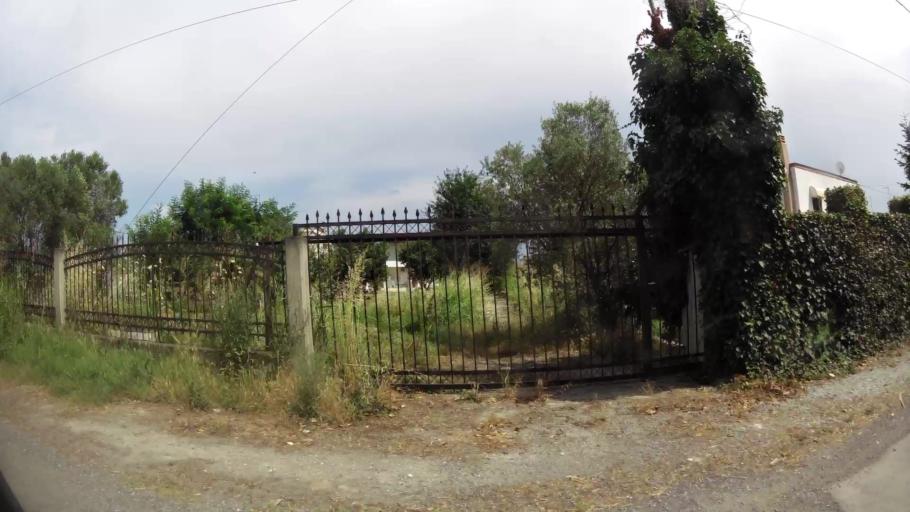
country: GR
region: Central Macedonia
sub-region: Nomos Pierias
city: Korinos
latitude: 40.3207
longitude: 22.5818
